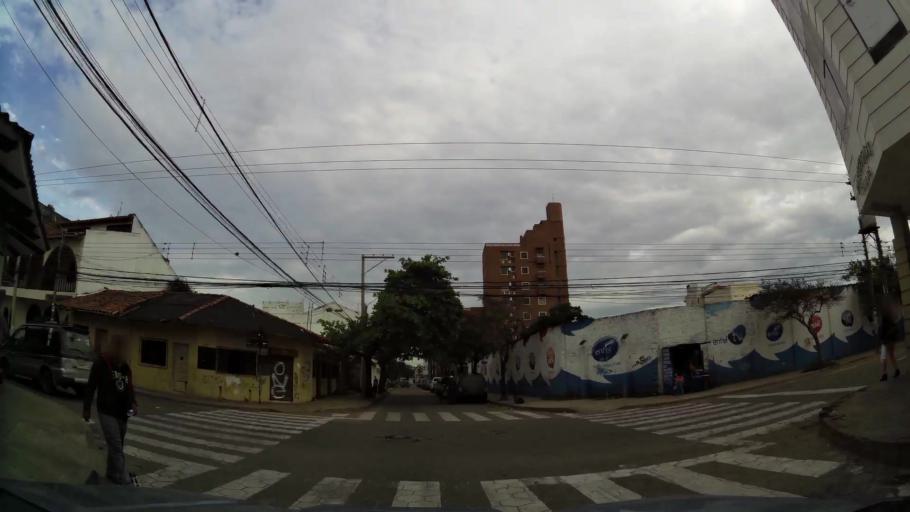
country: BO
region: Santa Cruz
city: Santa Cruz de la Sierra
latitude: -17.7833
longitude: -63.1762
